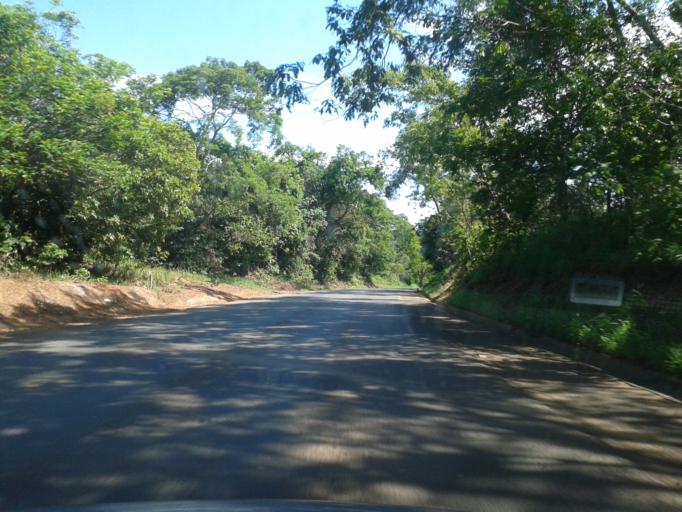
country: BR
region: Goias
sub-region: Piracanjuba
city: Piracanjuba
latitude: -17.2257
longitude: -48.7135
